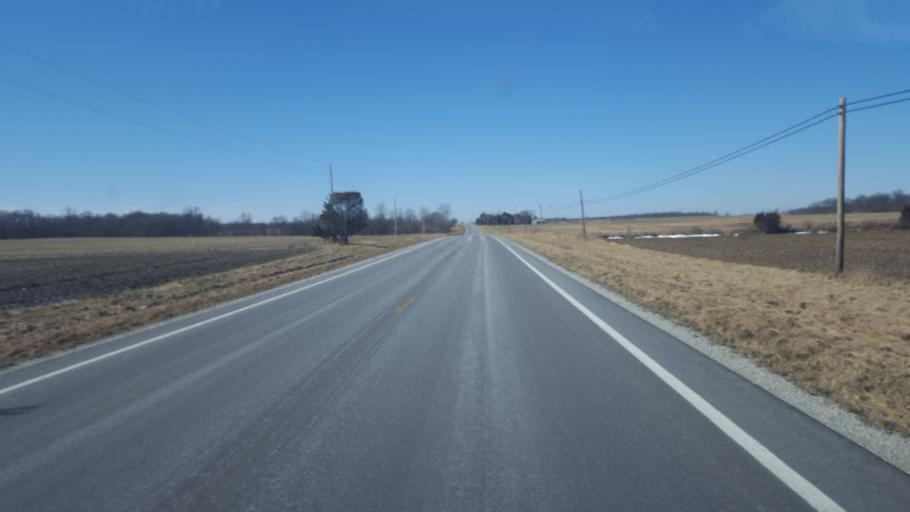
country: US
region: Ohio
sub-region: Hardin County
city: Kenton
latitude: 40.6439
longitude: -83.4426
